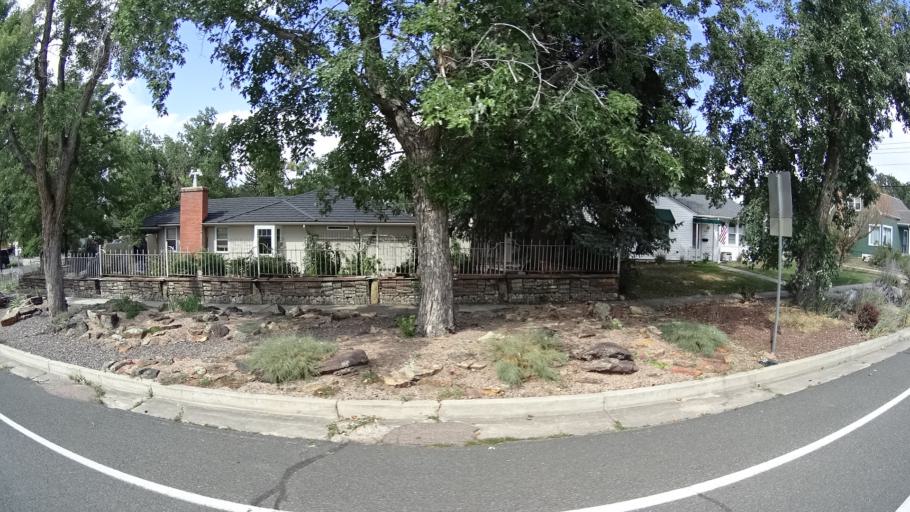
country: US
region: Colorado
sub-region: El Paso County
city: Colorado Springs
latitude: 38.8458
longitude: -104.7996
